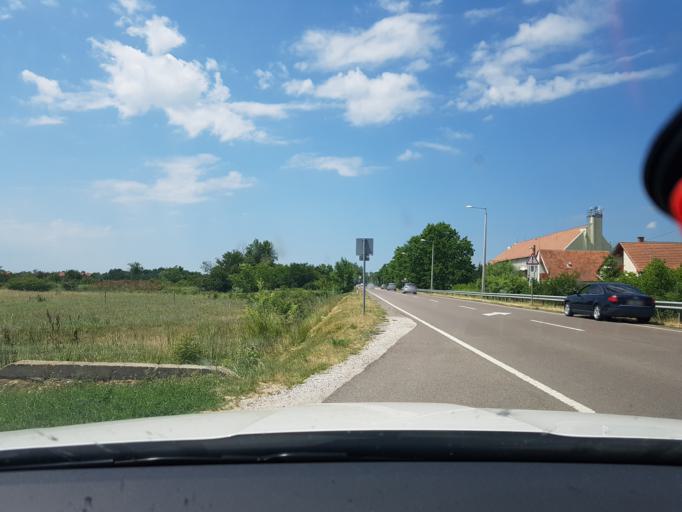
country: HU
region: Hajdu-Bihar
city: Hortobagy
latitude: 47.5816
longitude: 21.1586
